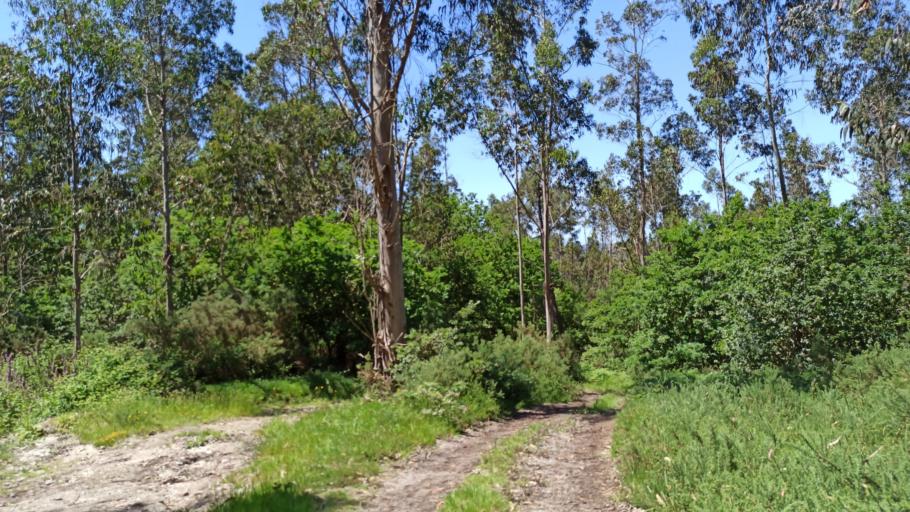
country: ES
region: Galicia
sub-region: Provincia da Coruna
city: Negreira
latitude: 42.9228
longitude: -8.7161
